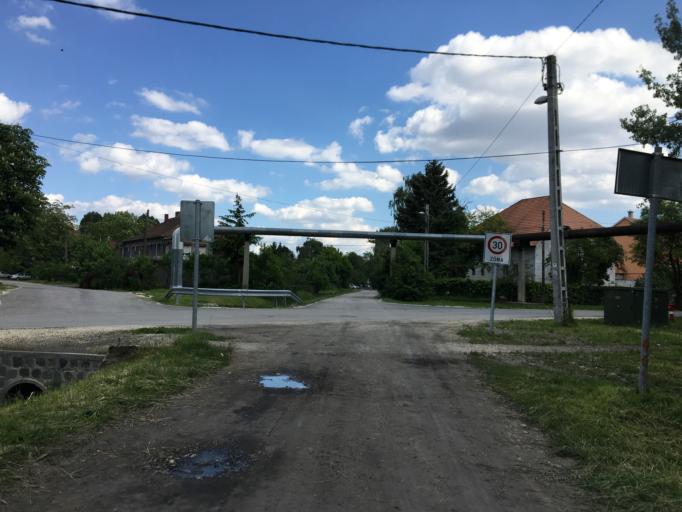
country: HU
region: Budapest
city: Budapest III. keruelet
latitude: 47.5708
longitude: 19.0439
